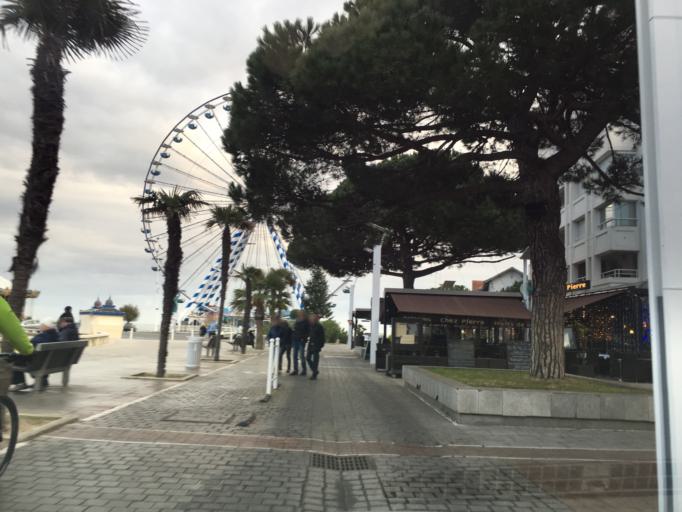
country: FR
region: Aquitaine
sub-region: Departement de la Gironde
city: Arcachon
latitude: 44.6636
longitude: -1.1645
